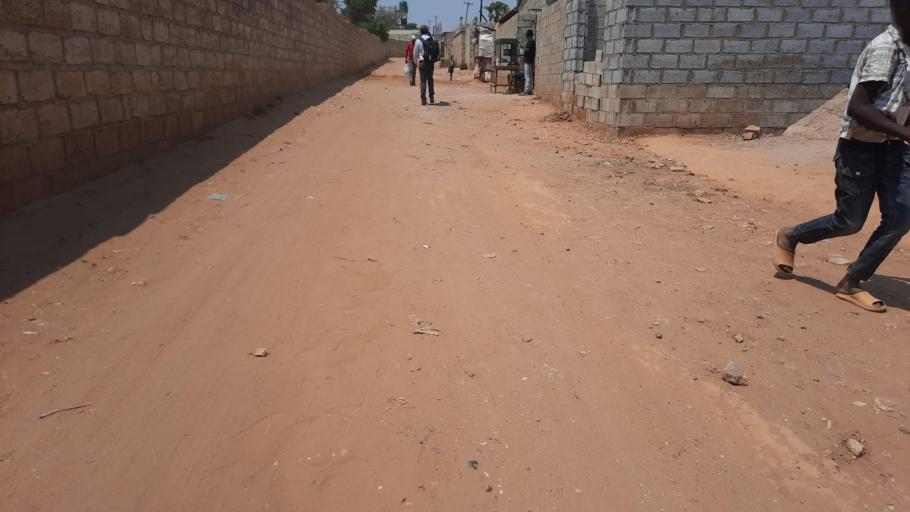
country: ZM
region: Lusaka
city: Lusaka
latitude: -15.4074
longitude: 28.3804
